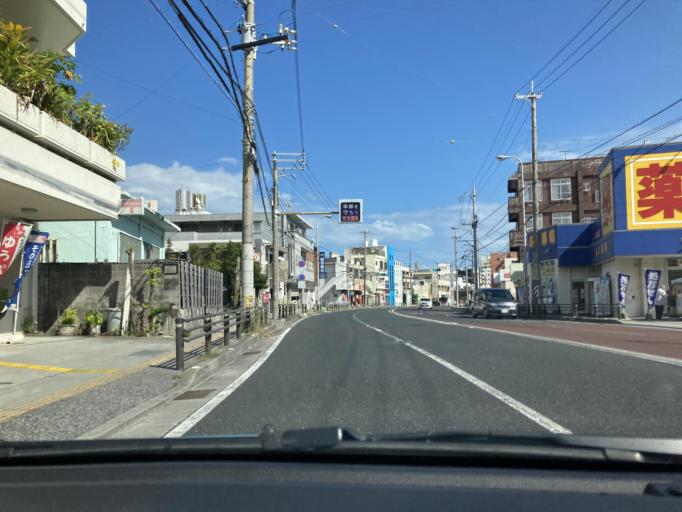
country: JP
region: Okinawa
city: Naha-shi
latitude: 26.1998
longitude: 127.6864
